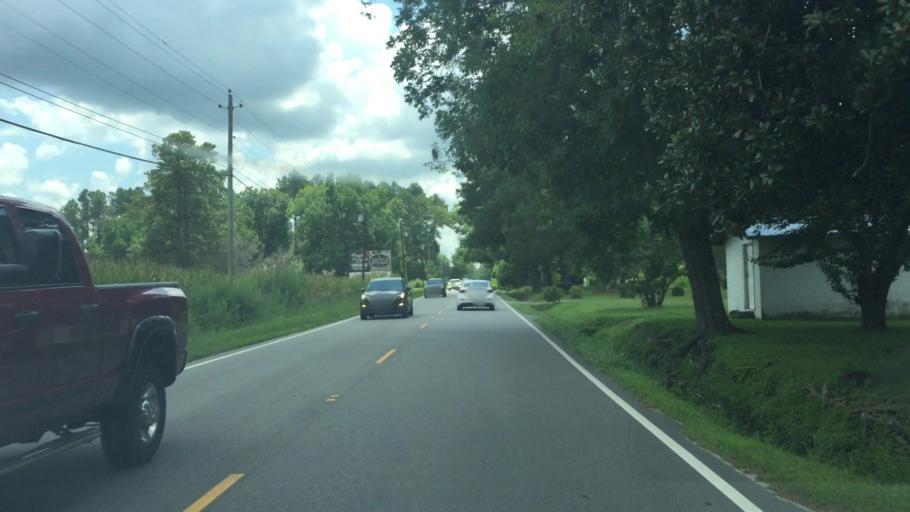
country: US
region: North Carolina
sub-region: Columbus County
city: Chadbourn
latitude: 34.3089
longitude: -78.8265
